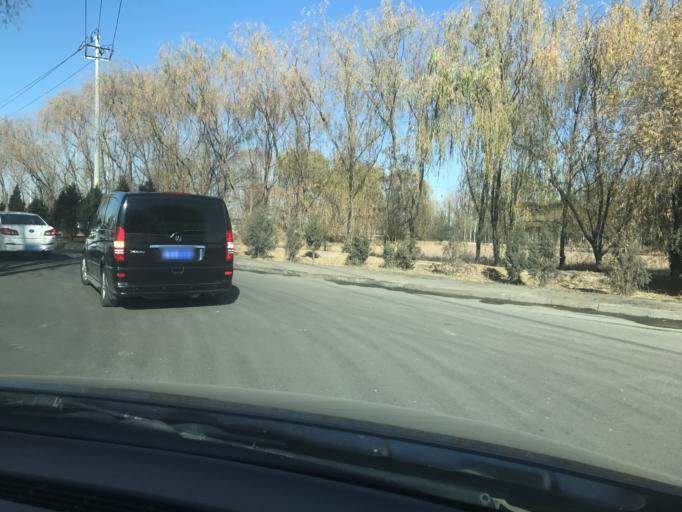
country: CN
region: Gansu Sheng
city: Gulang
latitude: 37.6810
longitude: 102.8370
